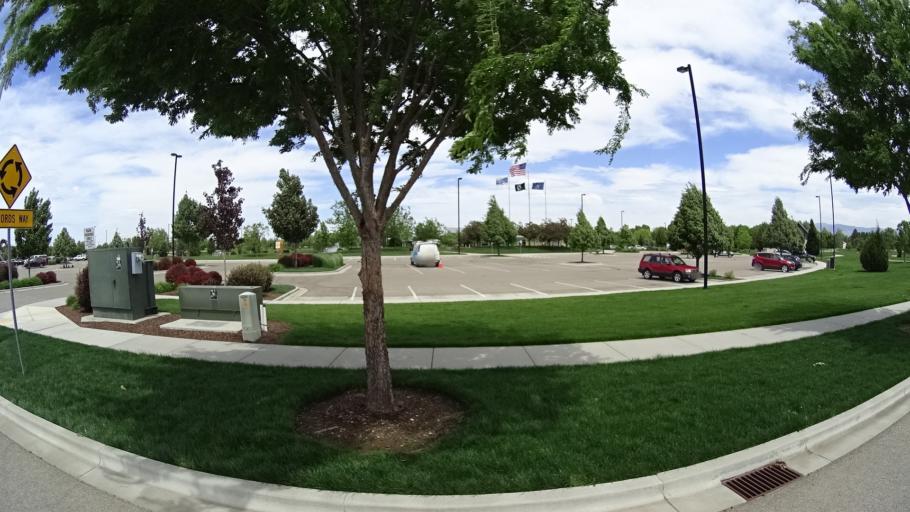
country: US
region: Idaho
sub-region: Ada County
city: Meridian
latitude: 43.6217
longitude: -116.3456
